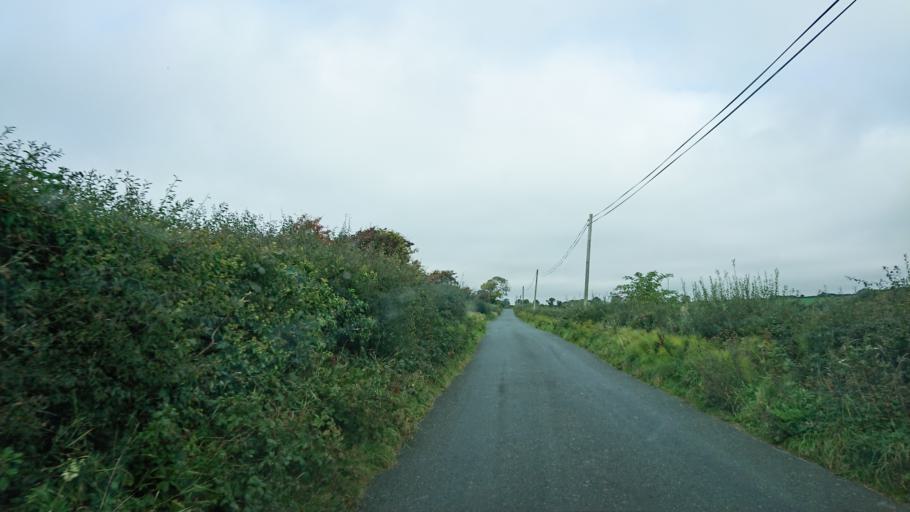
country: IE
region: Munster
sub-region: Waterford
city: Tra Mhor
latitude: 52.1855
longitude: -7.1156
